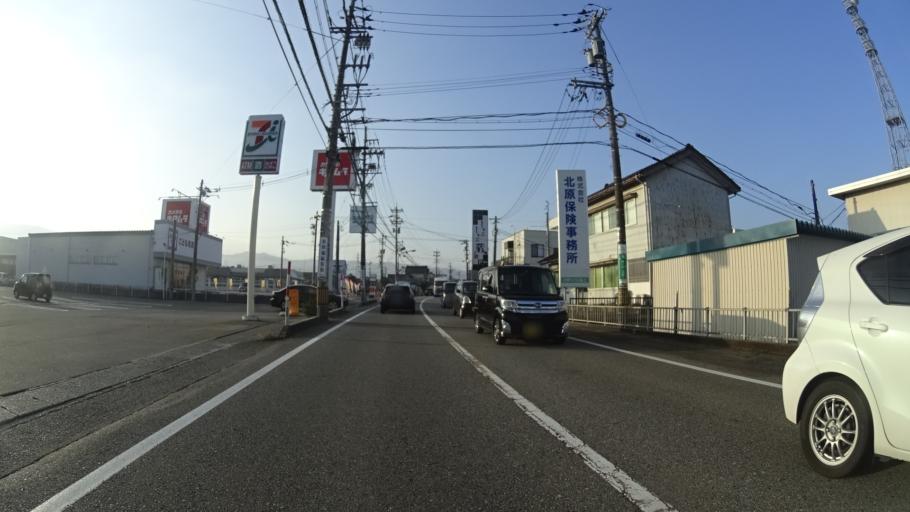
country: JP
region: Ishikawa
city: Nanao
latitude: 37.0351
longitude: 136.9686
